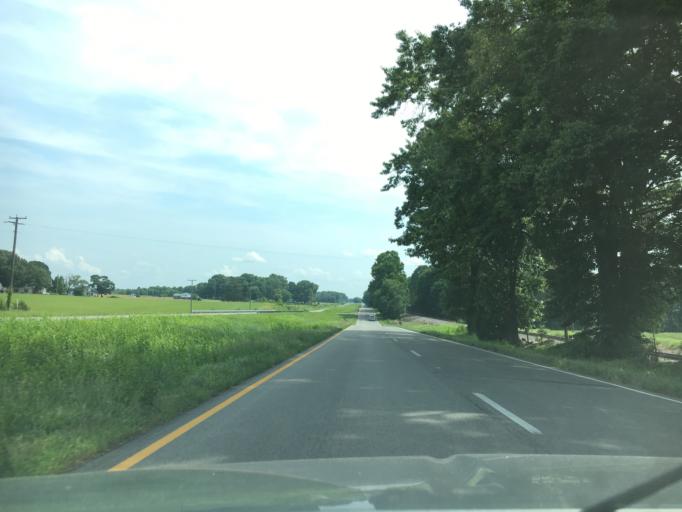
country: US
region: Virginia
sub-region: Nottoway County
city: Crewe
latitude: 37.2582
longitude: -78.1387
